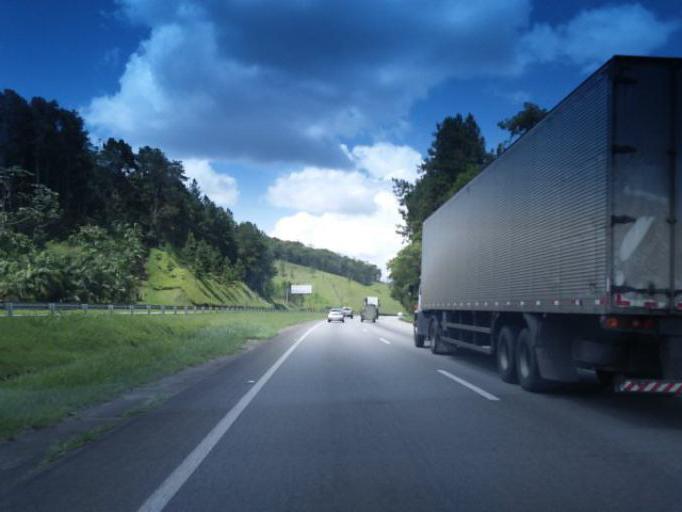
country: BR
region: Sao Paulo
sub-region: Juquitiba
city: Juquitiba
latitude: -23.9712
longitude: -47.1353
